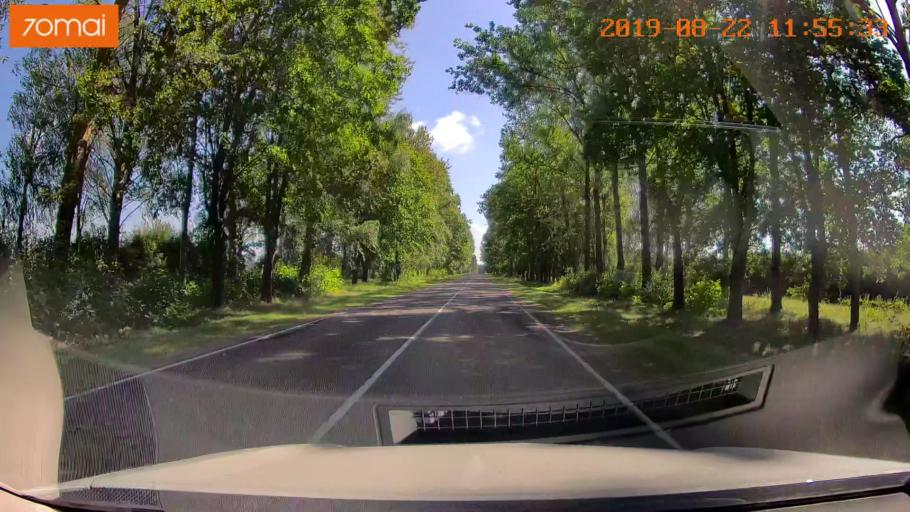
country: BY
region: Minsk
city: Prawdzinski
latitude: 53.4312
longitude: 27.5504
